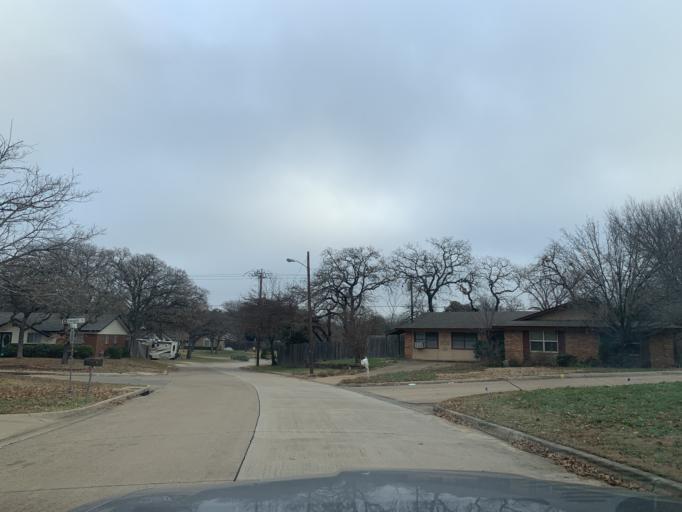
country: US
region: Texas
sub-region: Tarrant County
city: Hurst
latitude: 32.8312
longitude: -97.1556
